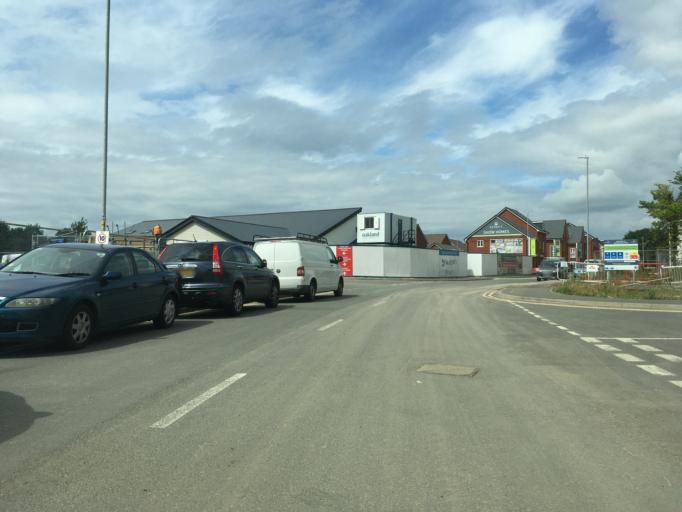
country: GB
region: England
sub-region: South Gloucestershire
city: Almondsbury
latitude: 51.5224
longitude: -2.5889
